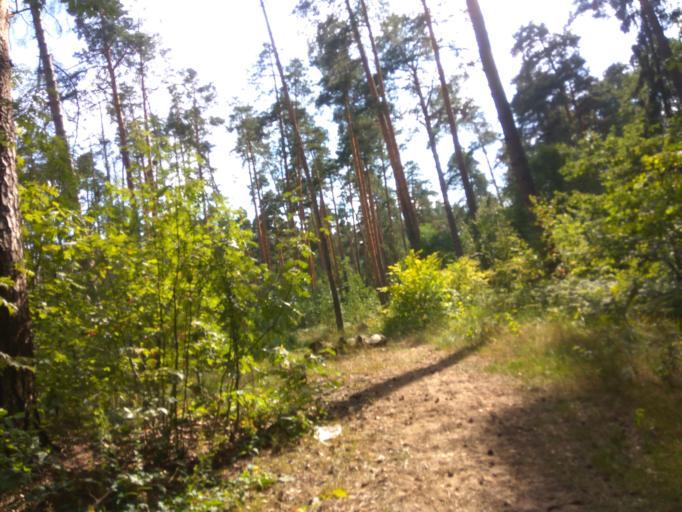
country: RU
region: Moskovskaya
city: Orekhovo-Zuyevo
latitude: 55.8275
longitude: 39.0266
